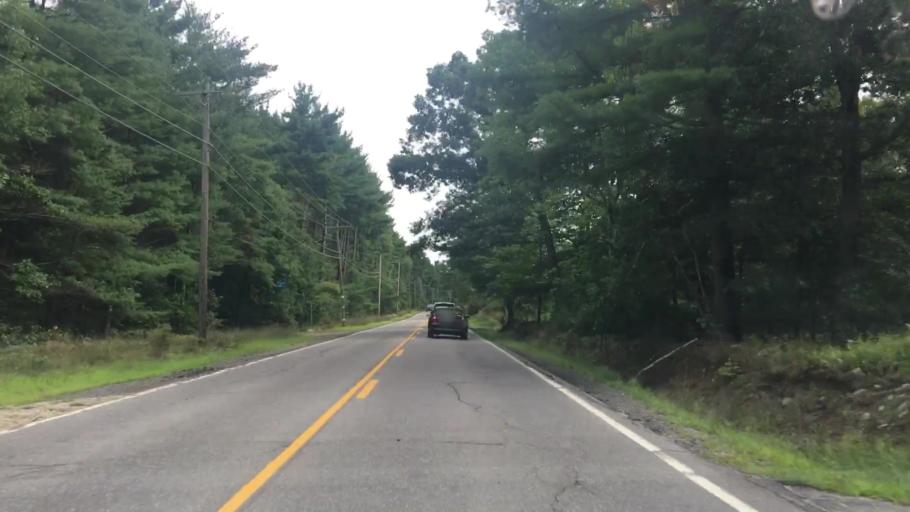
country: US
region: Maine
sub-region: York County
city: Lake Arrowhead
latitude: 43.6119
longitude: -70.7178
